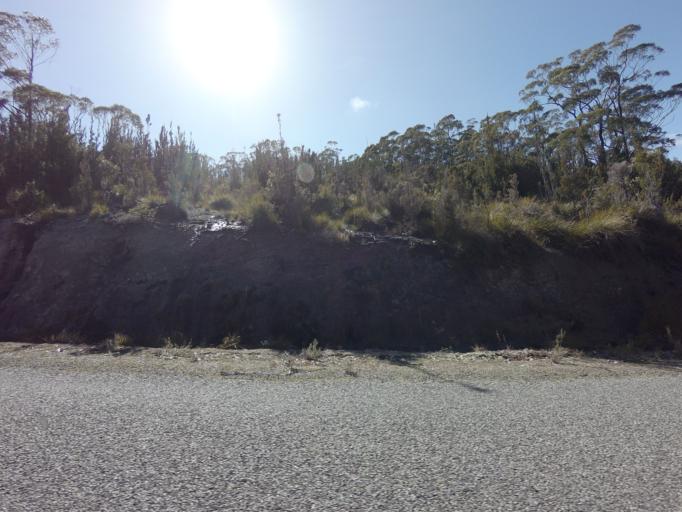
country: AU
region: Tasmania
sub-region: Derwent Valley
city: New Norfolk
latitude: -42.7635
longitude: 146.3968
